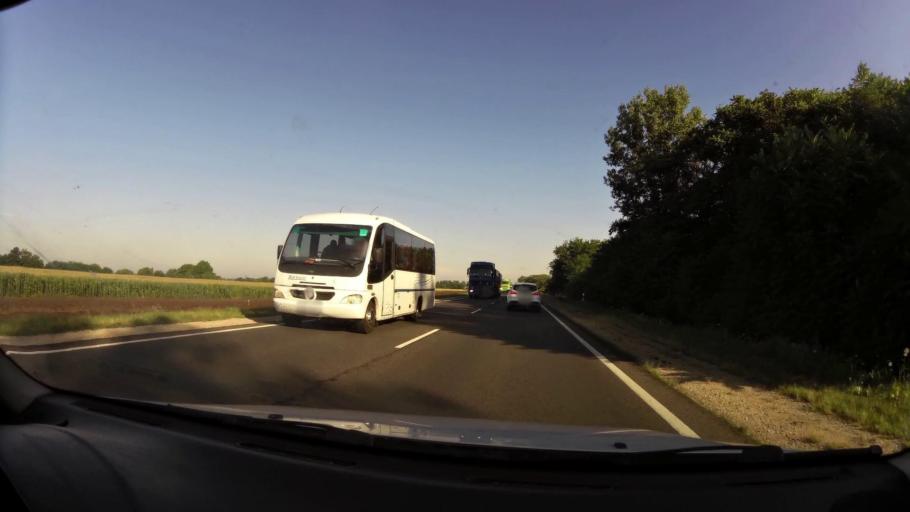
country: HU
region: Pest
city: Albertirsa
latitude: 47.2498
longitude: 19.6441
